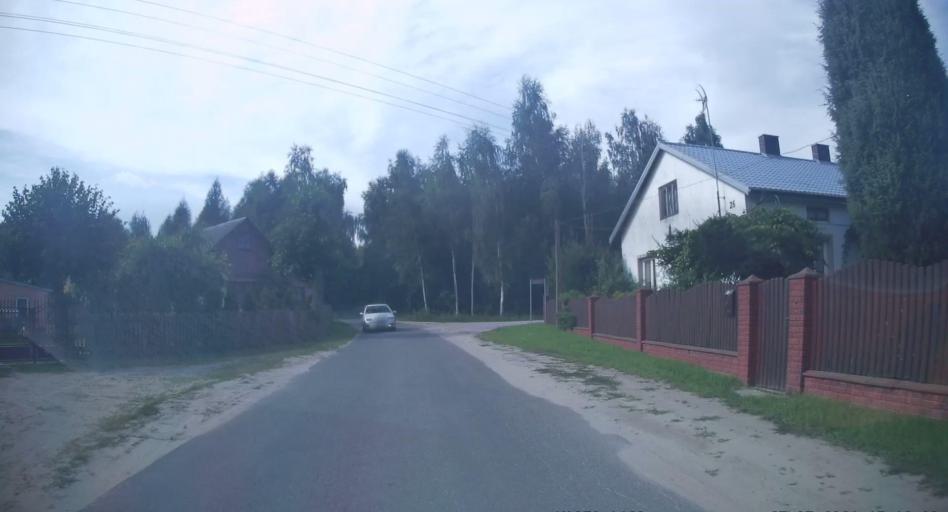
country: PL
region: Lodz Voivodeship
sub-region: Powiat rawski
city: Rawa Mazowiecka
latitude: 51.6948
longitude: 20.2518
